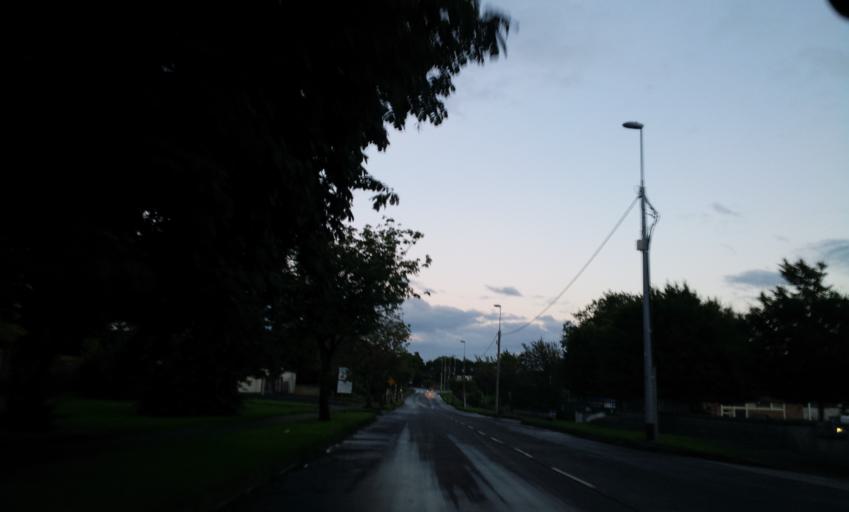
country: IE
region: Munster
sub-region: County Limerick
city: Luimneach
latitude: 52.6553
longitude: -8.6484
